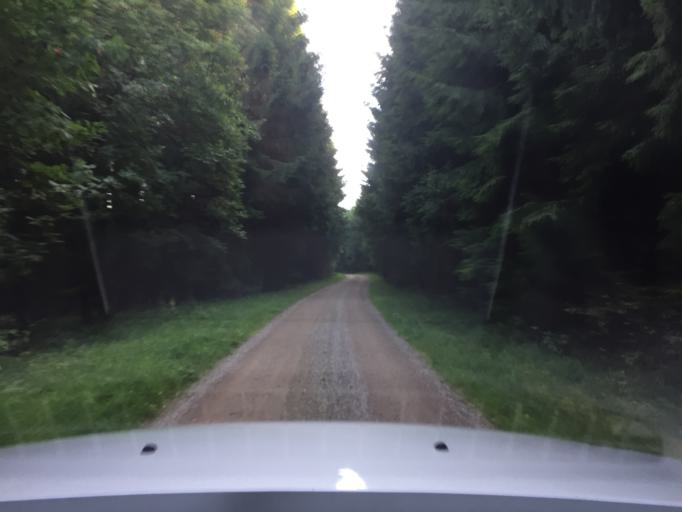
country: SE
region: Skane
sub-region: Hassleholms Kommun
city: Sosdala
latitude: 56.0144
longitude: 13.7078
